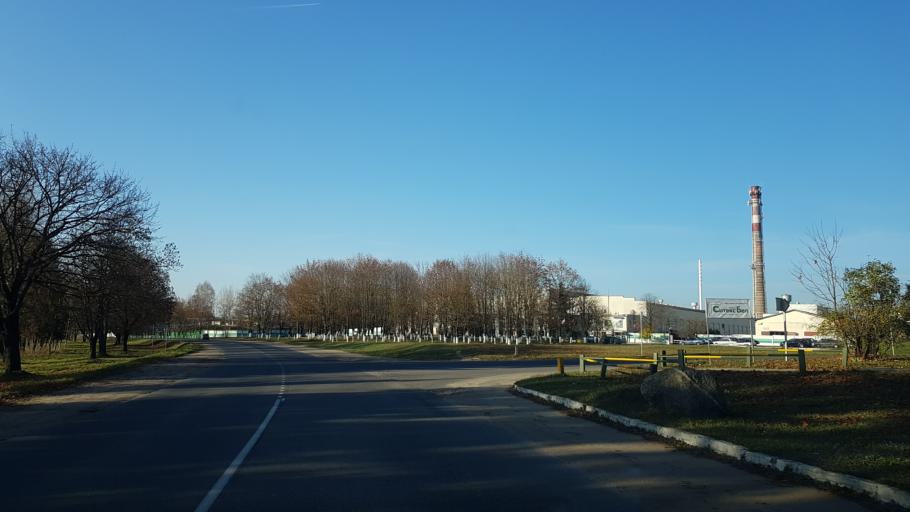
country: BY
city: Fanipol
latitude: 53.7342
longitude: 27.3302
